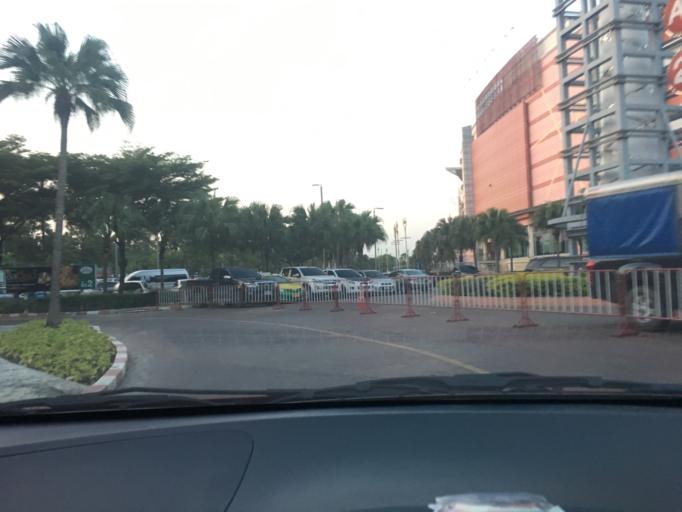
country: TH
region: Bangkok
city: Bang Khun Thian
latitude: 13.6618
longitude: 100.4373
